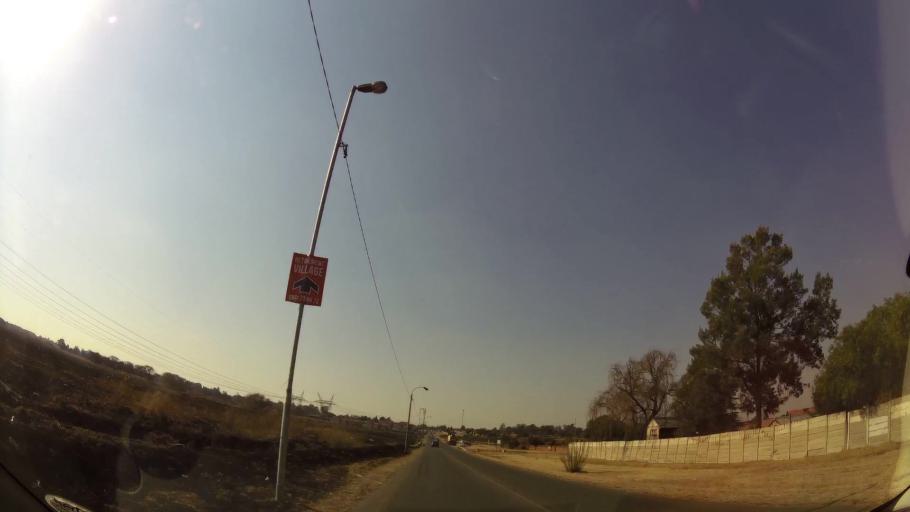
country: ZA
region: Gauteng
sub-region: Ekurhuleni Metropolitan Municipality
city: Benoni
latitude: -26.1422
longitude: 28.2839
